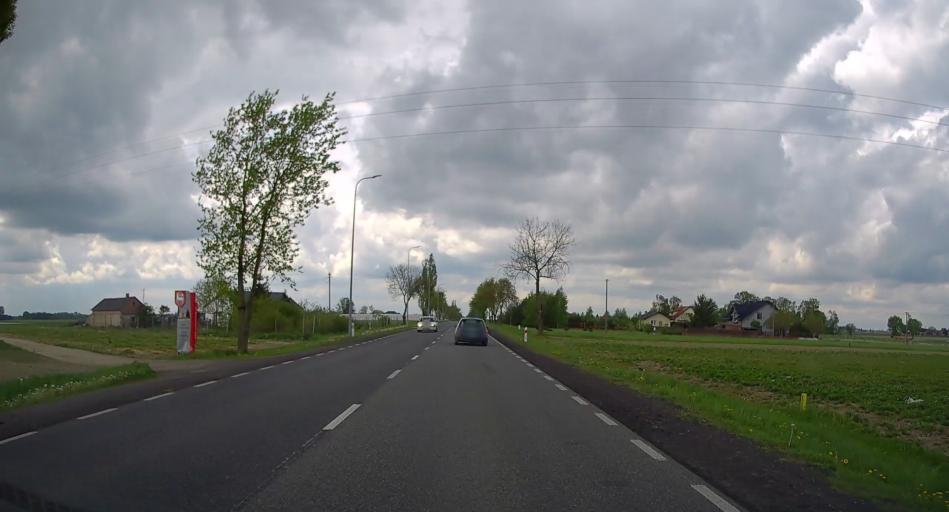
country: PL
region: Masovian Voivodeship
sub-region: Powiat plonski
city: Zaluski
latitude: 52.4425
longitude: 20.4897
